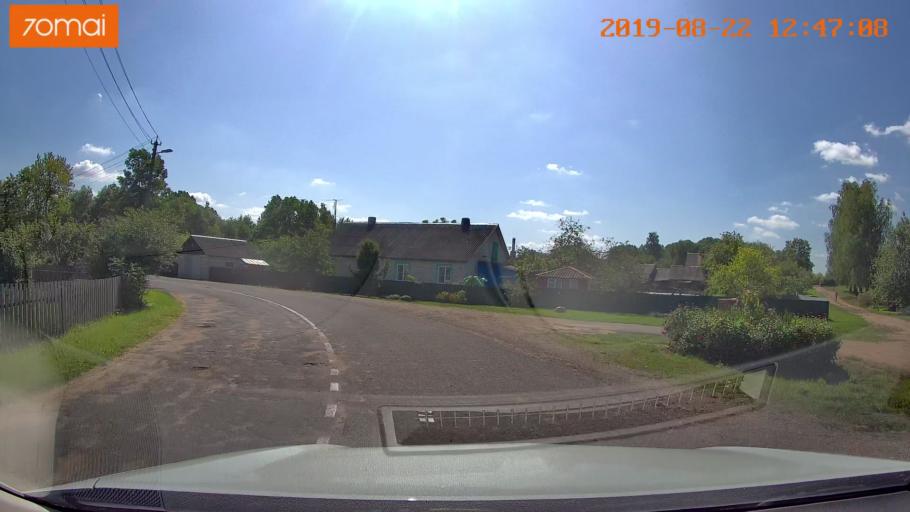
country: BY
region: Minsk
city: Prawdzinski
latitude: 53.4573
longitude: 27.6367
